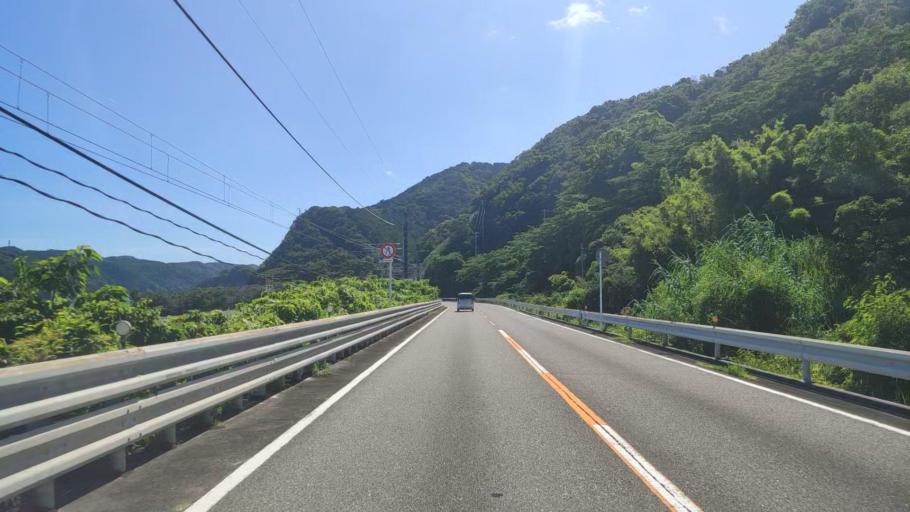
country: JP
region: Wakayama
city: Shingu
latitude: 33.5692
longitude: 135.9114
